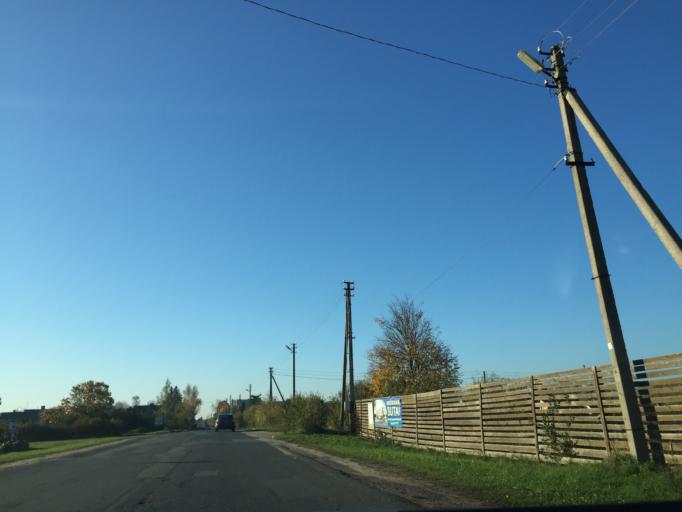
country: LT
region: Klaipedos apskritis
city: Kretinga
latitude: 55.8936
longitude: 21.2189
